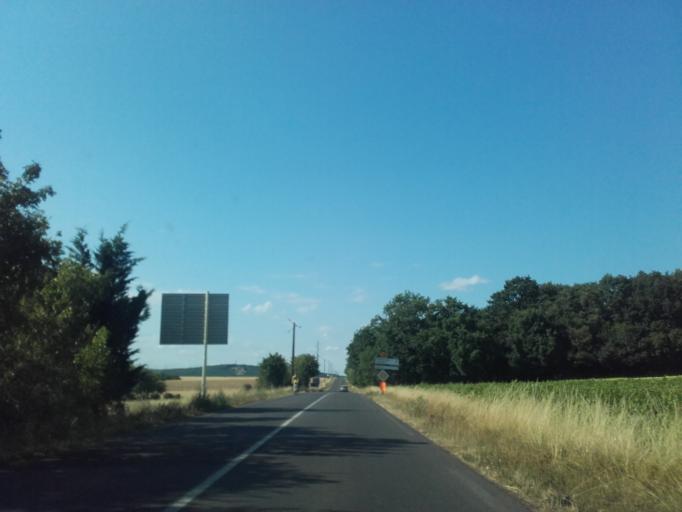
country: FR
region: Bourgogne
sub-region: Departement de Saone-et-Loire
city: Dracy-le-Fort
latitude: 46.8176
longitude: 4.7520
